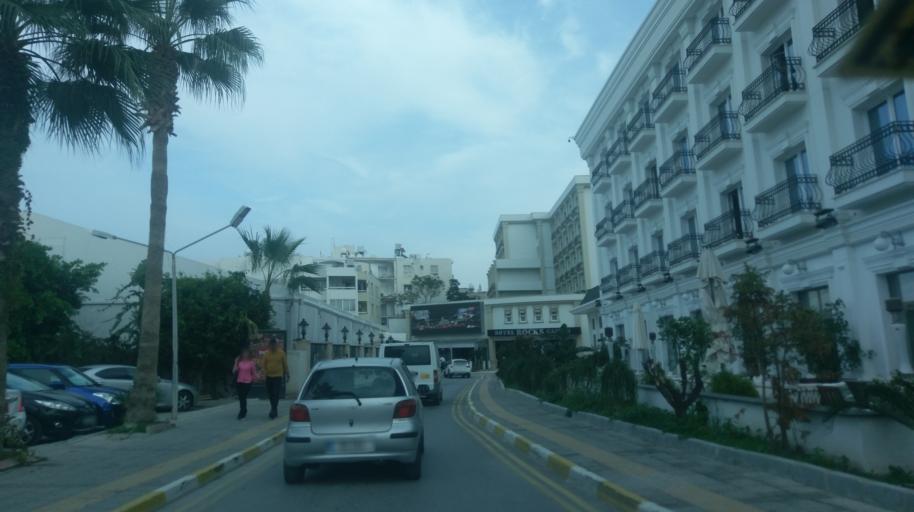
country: CY
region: Keryneia
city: Kyrenia
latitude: 35.3405
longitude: 33.3142
